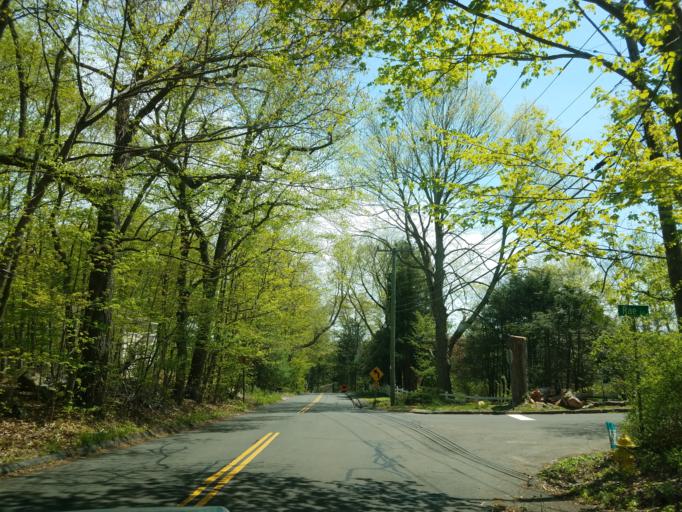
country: US
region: Connecticut
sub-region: Fairfield County
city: Norwalk
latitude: 41.1395
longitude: -73.4337
